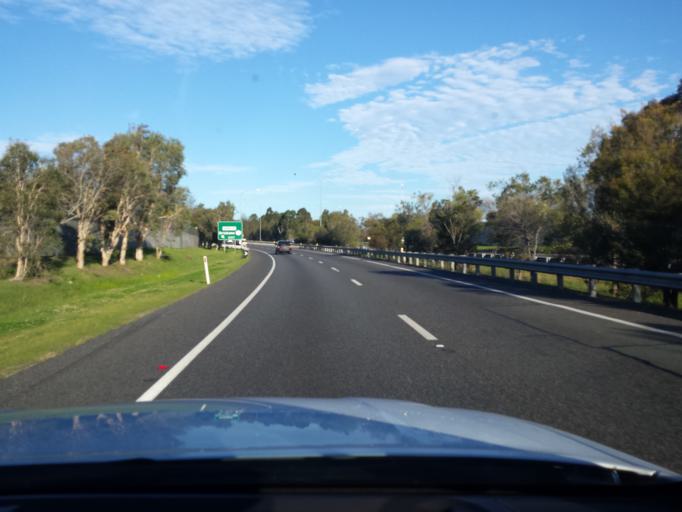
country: AU
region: Queensland
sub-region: Logan
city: Beenleigh
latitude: -27.6835
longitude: 153.1738
